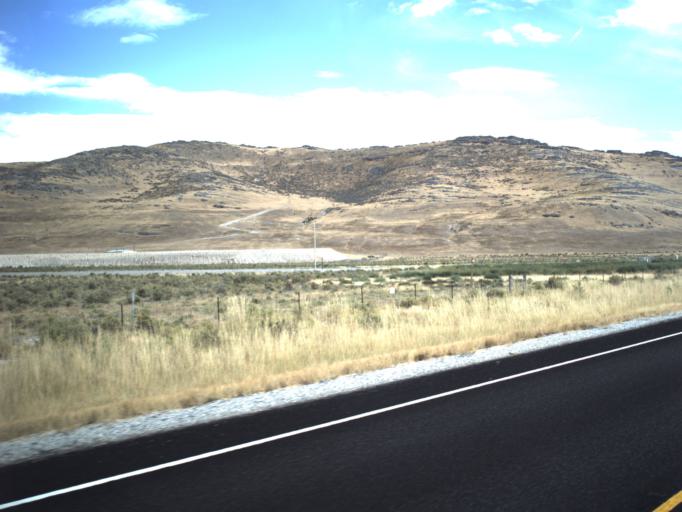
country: US
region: Utah
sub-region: Box Elder County
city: Tremonton
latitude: 41.6259
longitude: -112.3960
